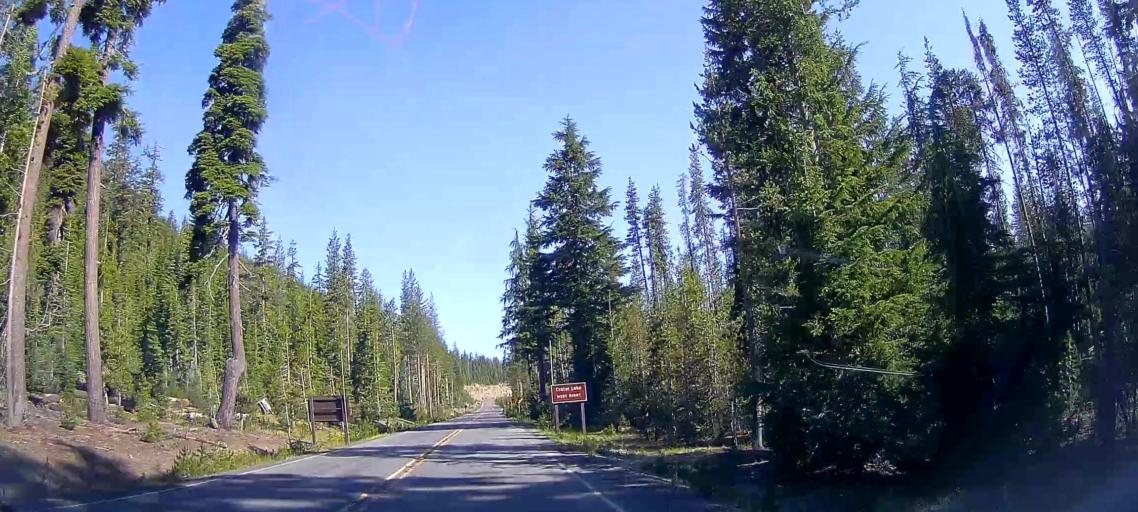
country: US
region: Oregon
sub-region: Jackson County
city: Shady Cove
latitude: 42.8632
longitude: -122.1672
